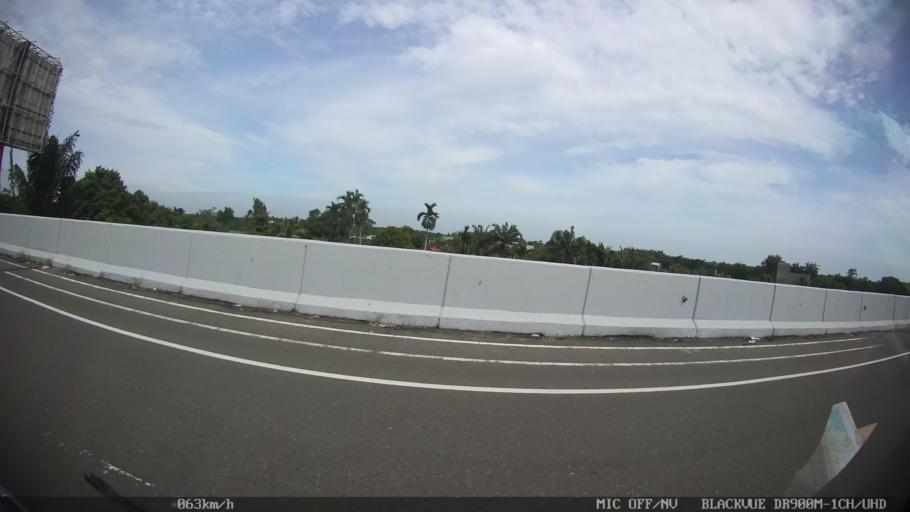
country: ID
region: North Sumatra
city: Percut
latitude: 3.6091
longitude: 98.8526
